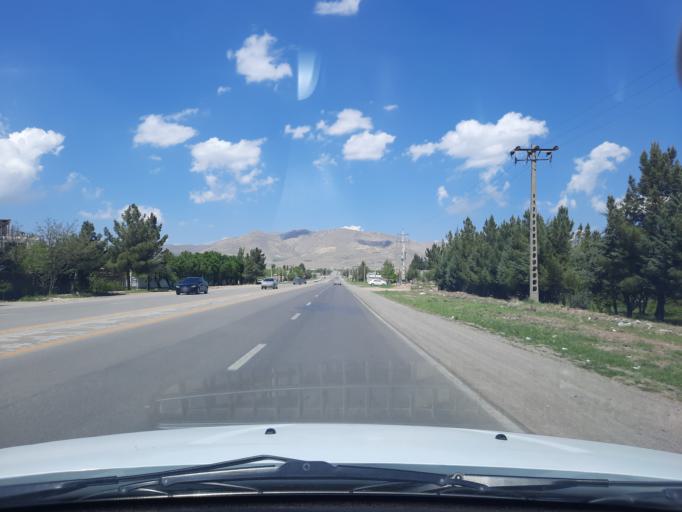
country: IR
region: Qazvin
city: Alvand
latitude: 36.3055
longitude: 50.1443
